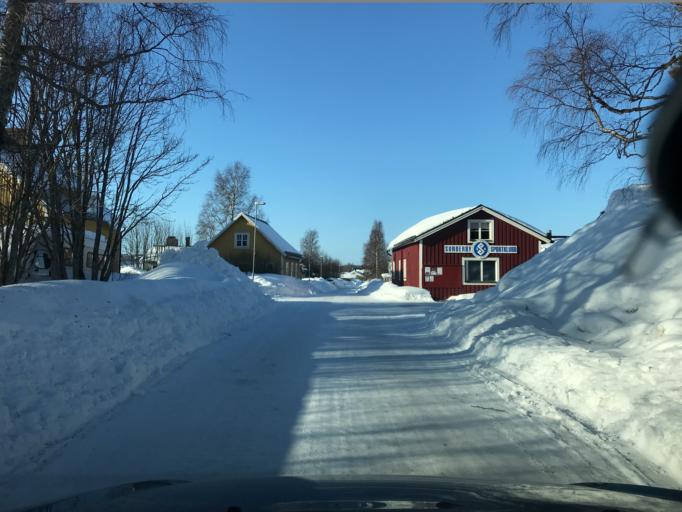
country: SE
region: Norrbotten
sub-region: Lulea Kommun
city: Sodra Sunderbyn
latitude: 65.6589
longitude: 21.9388
